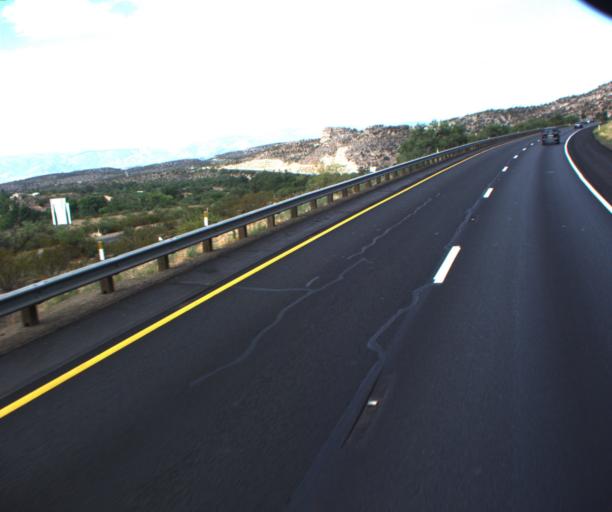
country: US
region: Arizona
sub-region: Yavapai County
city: Lake Montezuma
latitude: 34.6365
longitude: -111.8247
